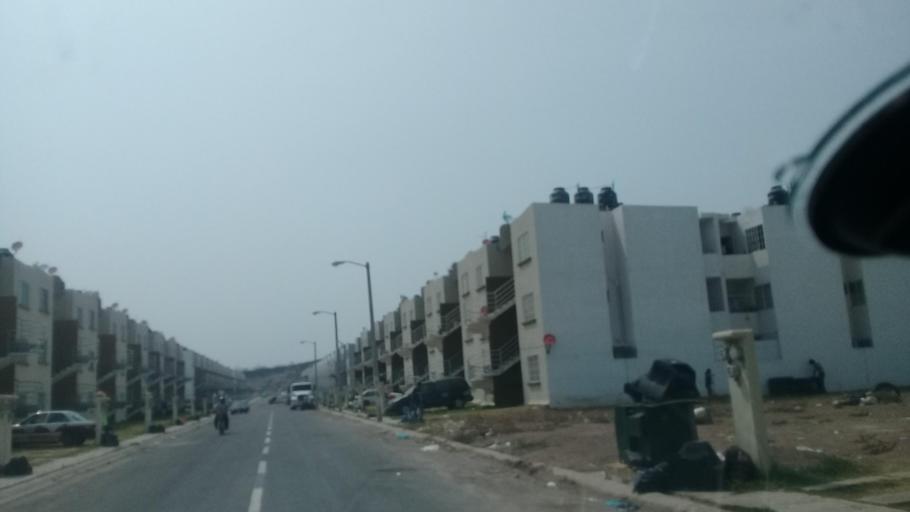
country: MX
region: Veracruz
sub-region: Veracruz
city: Lomas de Rio Medio Cuatro
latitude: 19.1816
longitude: -96.2107
